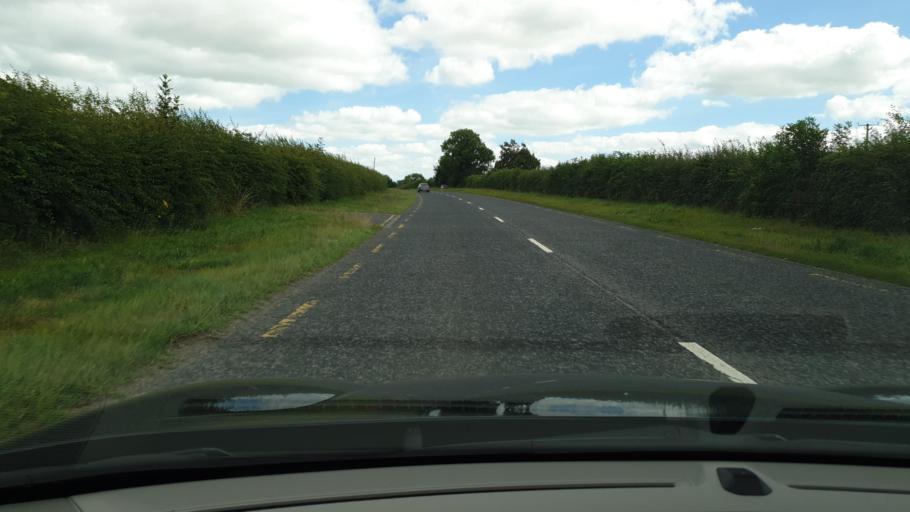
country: IE
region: Leinster
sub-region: An Mhi
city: Newtown Trim
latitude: 53.5353
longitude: -6.7063
